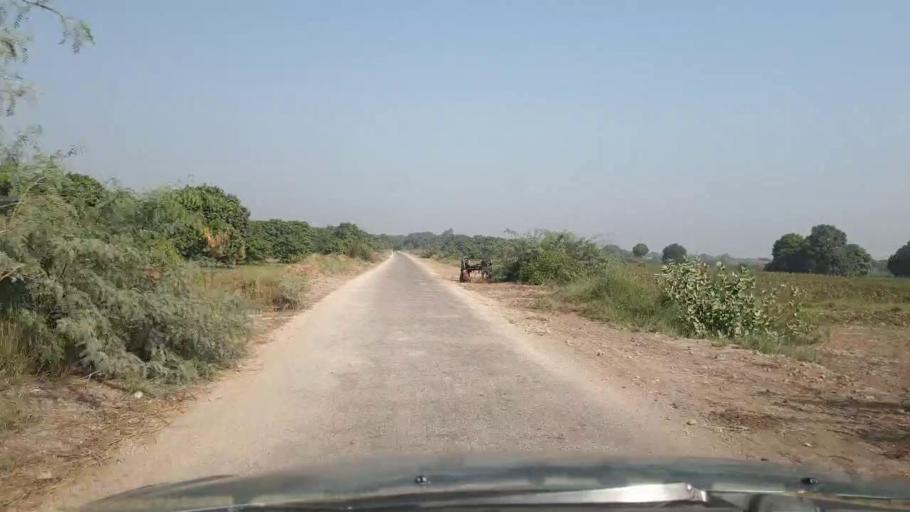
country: PK
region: Sindh
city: Tando Jam
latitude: 25.3238
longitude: 68.5404
